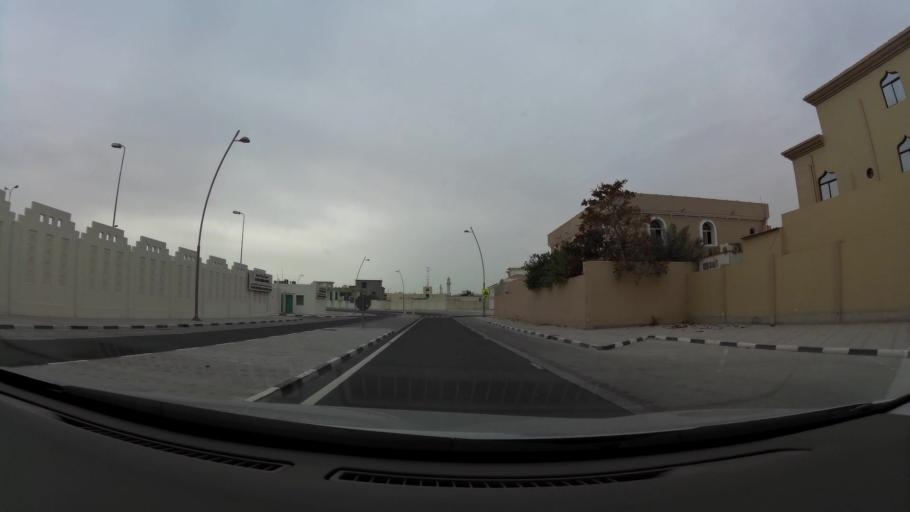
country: QA
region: Baladiyat ad Dawhah
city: Doha
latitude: 25.3461
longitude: 51.4949
